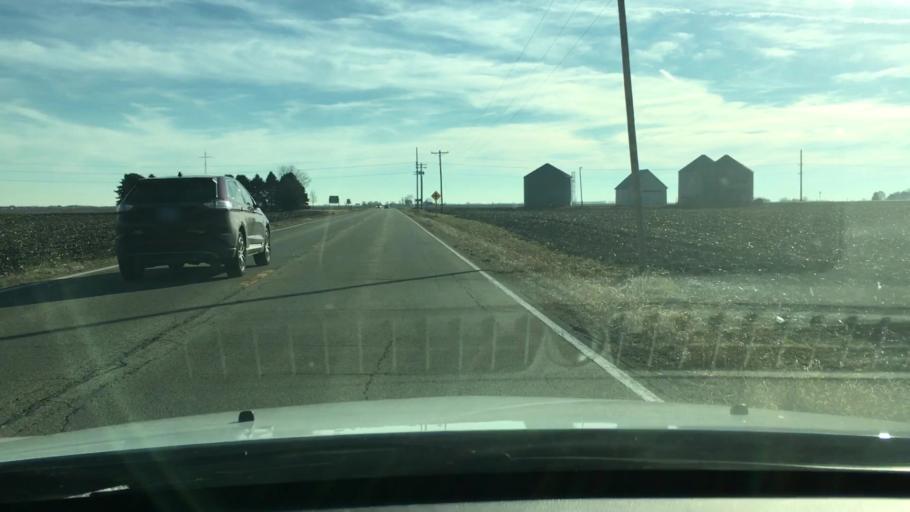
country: US
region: Illinois
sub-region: LaSalle County
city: Mendota
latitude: 41.4422
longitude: -89.1268
